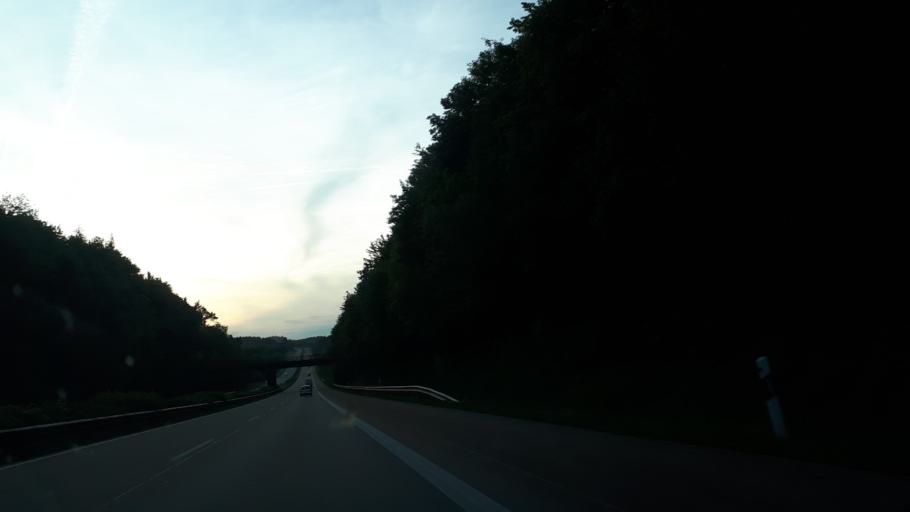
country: DE
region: Rheinland-Pfalz
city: Laubach
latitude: 50.2262
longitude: 7.1004
